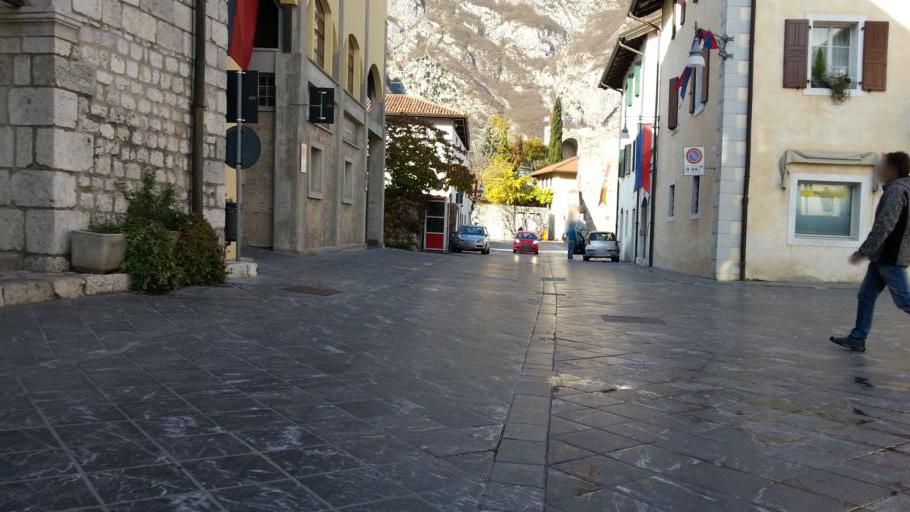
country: IT
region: Friuli Venezia Giulia
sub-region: Provincia di Udine
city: Venzone
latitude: 46.3338
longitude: 13.1391
